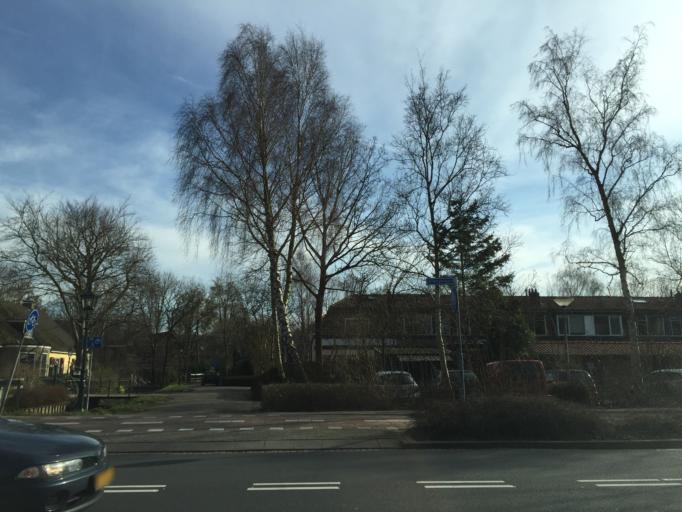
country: NL
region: South Holland
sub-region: Gemeente Pijnacker-Nootdorp
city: Pijnacker
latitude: 52.0119
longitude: 4.4337
